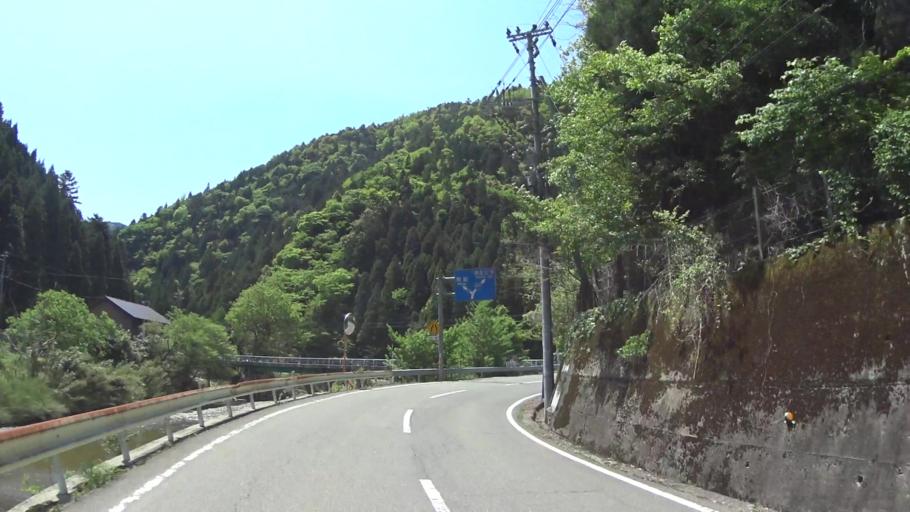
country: JP
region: Shiga Prefecture
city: Kitahama
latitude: 35.2057
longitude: 135.7476
